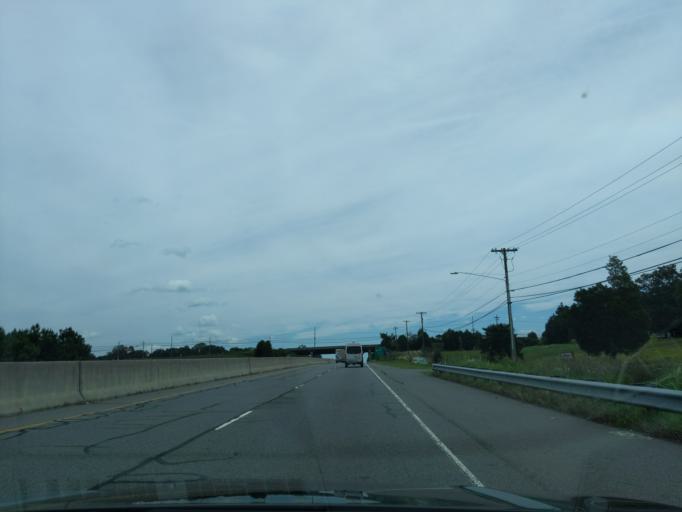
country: US
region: North Carolina
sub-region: Cabarrus County
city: Concord
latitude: 35.3726
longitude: -80.5543
